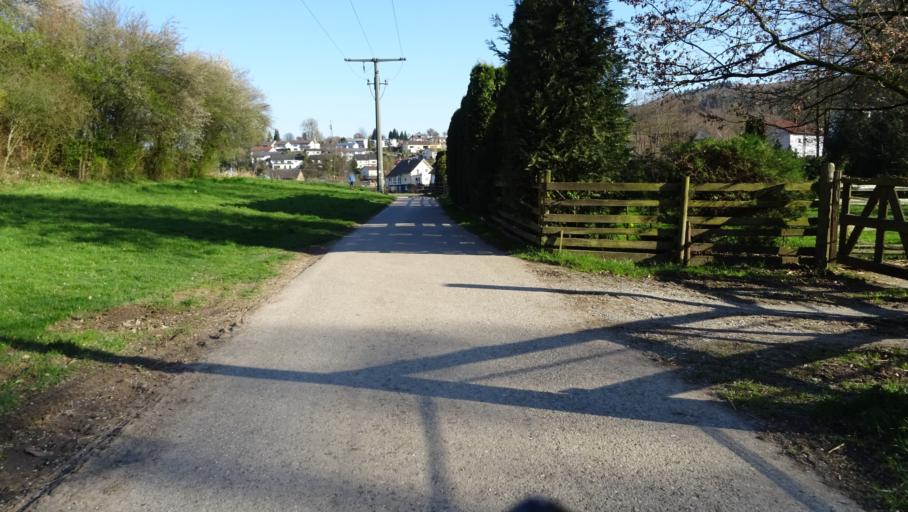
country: DE
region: Baden-Wuerttemberg
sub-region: Karlsruhe Region
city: Obrigheim
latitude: 49.3526
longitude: 9.0809
